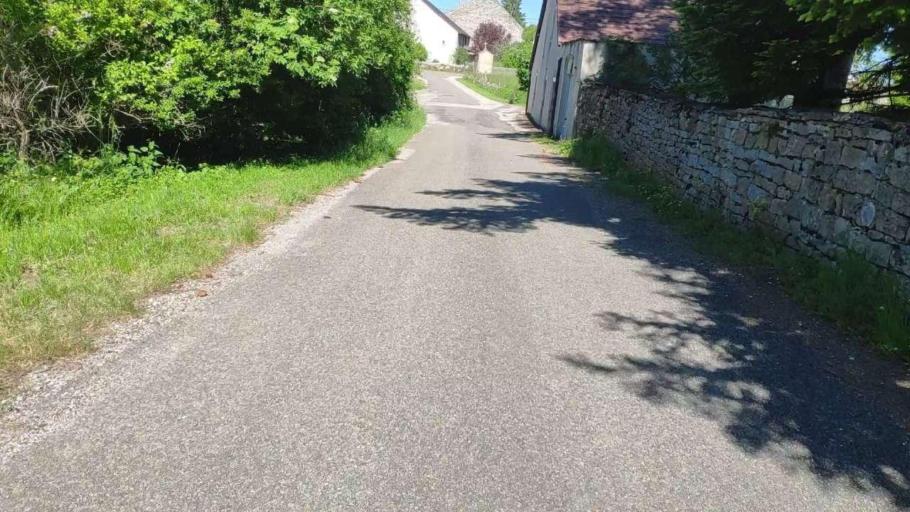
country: FR
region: Franche-Comte
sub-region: Departement du Jura
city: Clairvaux-les-Lacs
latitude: 46.6995
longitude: 5.7305
